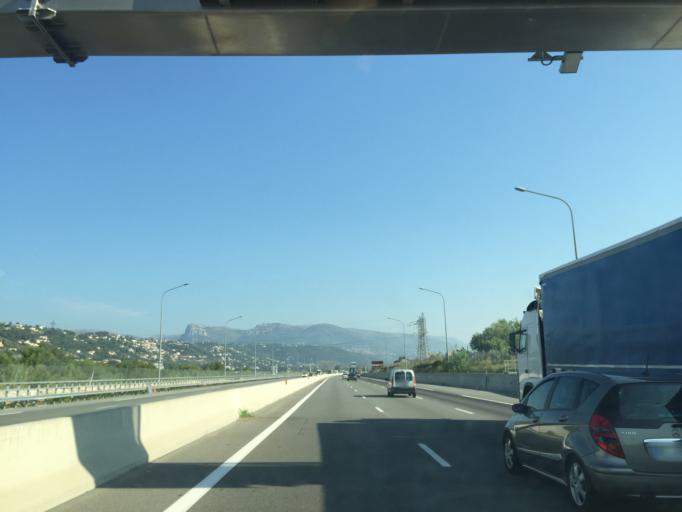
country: FR
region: Provence-Alpes-Cote d'Azur
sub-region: Departement des Alpes-Maritimes
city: Saint-Laurent-du-Var
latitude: 43.6825
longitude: 7.1926
